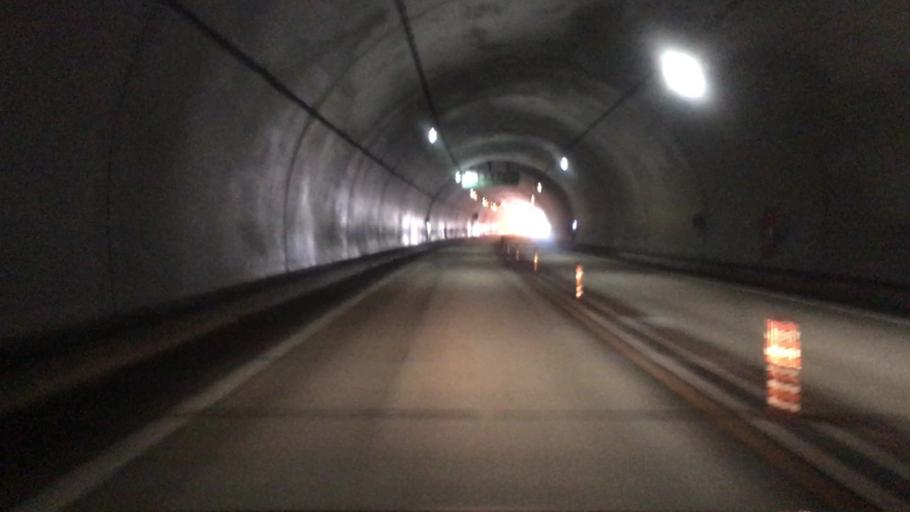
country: JP
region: Tottori
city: Tottori
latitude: 35.6036
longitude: 134.3749
